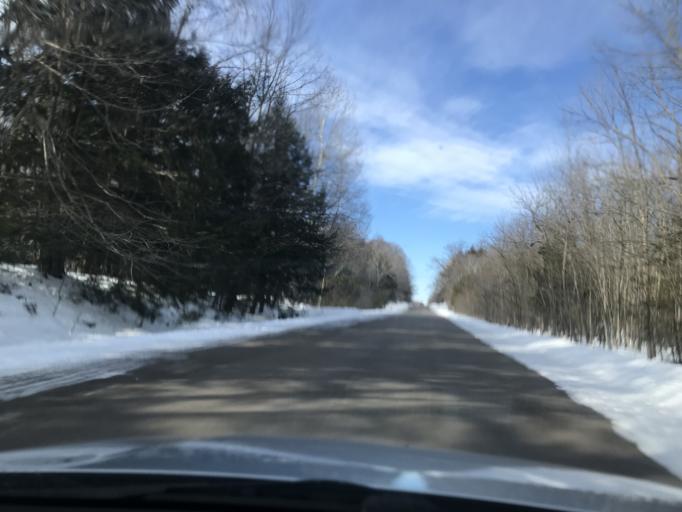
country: US
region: Wisconsin
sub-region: Oconto County
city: Gillett
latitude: 44.9616
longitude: -88.2781
